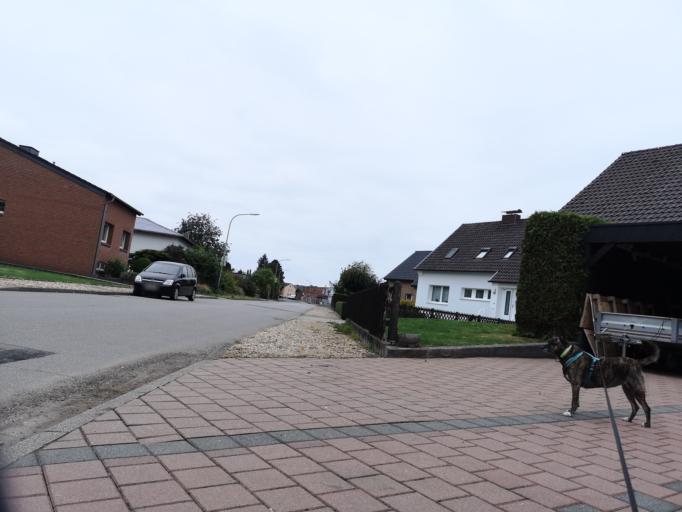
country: DE
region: North Rhine-Westphalia
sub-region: Regierungsbezirk Koln
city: Kreuzau
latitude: 50.7490
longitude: 6.4945
